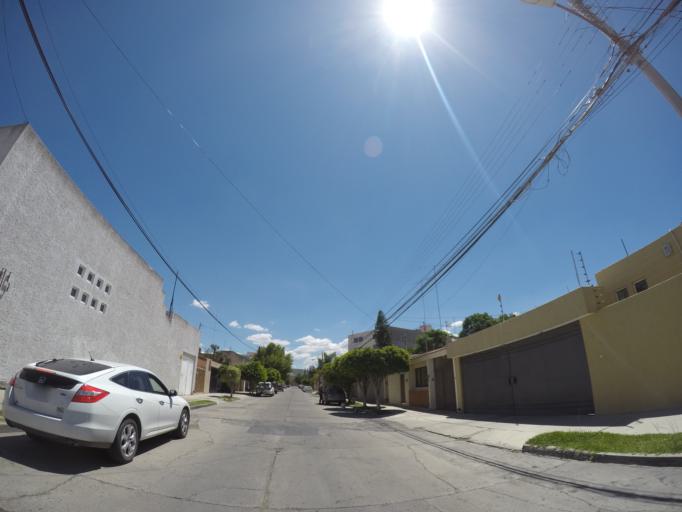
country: MX
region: San Luis Potosi
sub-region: San Luis Potosi
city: San Luis Potosi
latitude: 22.1445
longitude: -101.0086
